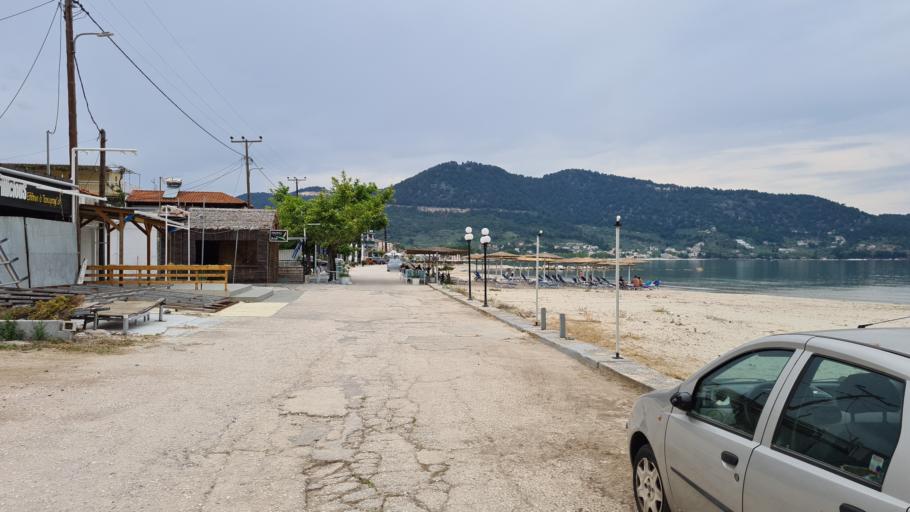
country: GR
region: East Macedonia and Thrace
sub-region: Nomos Kavalas
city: Potamia
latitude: 40.7090
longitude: 24.7598
